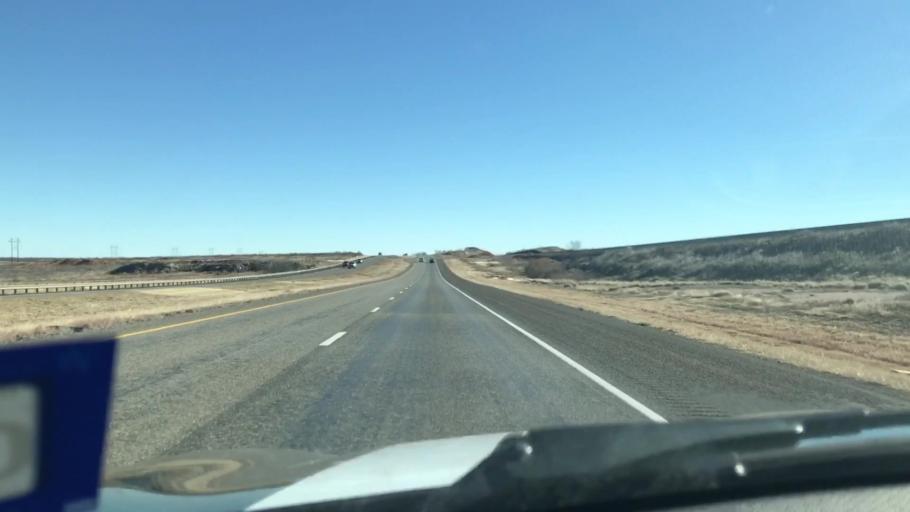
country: US
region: Texas
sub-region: Garza County
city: Post
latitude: 33.1128
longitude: -101.2734
